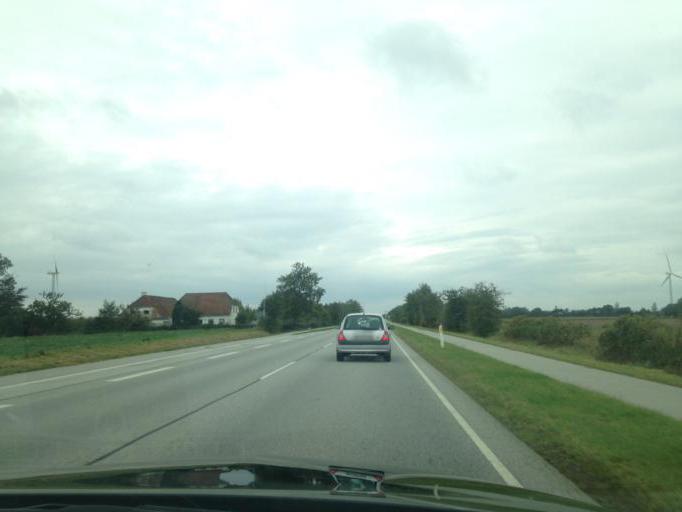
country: DK
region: South Denmark
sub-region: Kolding Kommune
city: Christiansfeld
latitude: 55.3186
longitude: 9.4959
